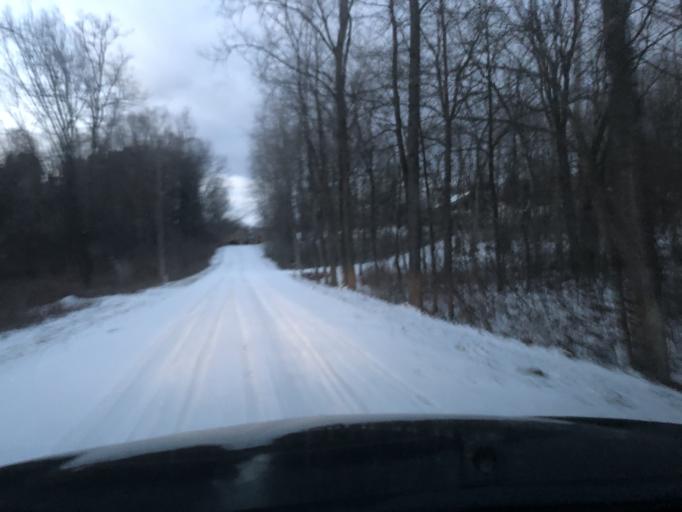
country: US
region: Michigan
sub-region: Oakland County
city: Milford
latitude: 42.5759
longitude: -83.6490
